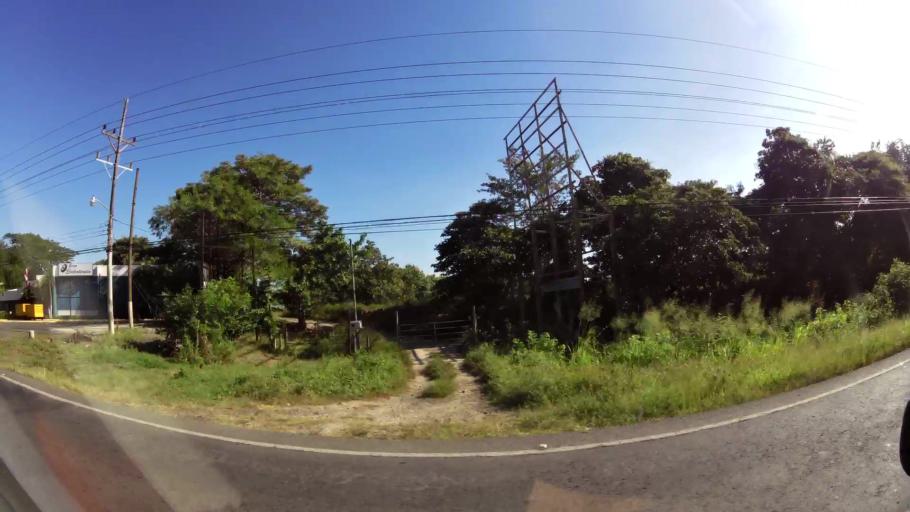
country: CR
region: Guanacaste
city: Sardinal
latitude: 10.5810
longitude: -85.5705
